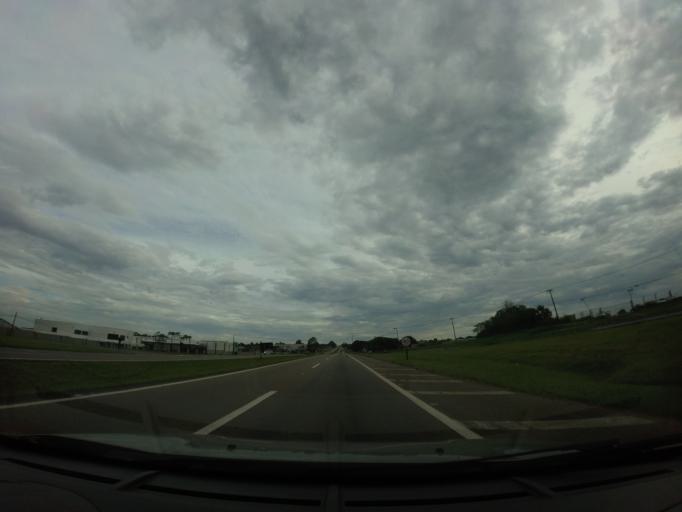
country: BR
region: Sao Paulo
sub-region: Piracicaba
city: Piracicaba
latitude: -22.7432
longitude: -47.6003
